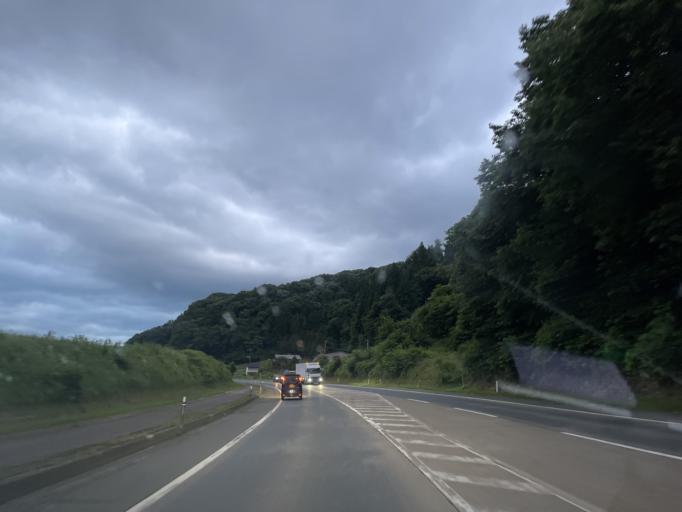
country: JP
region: Iwate
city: Morioka-shi
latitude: 39.9269
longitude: 141.1950
